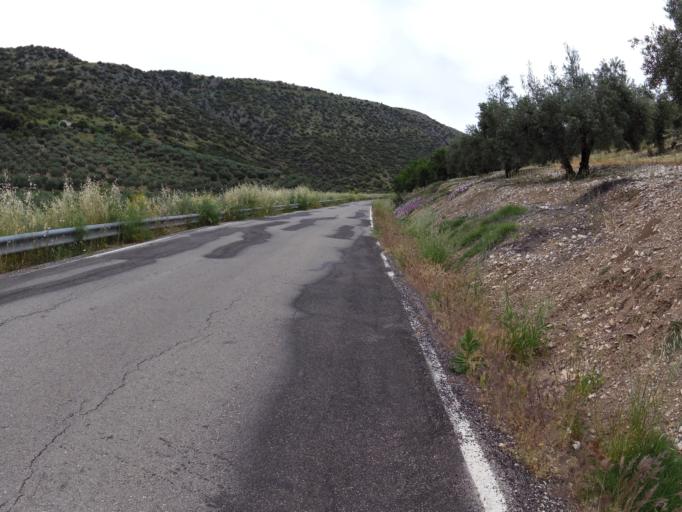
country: ES
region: Andalusia
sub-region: Province of Cordoba
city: Luque
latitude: 37.5186
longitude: -4.2204
